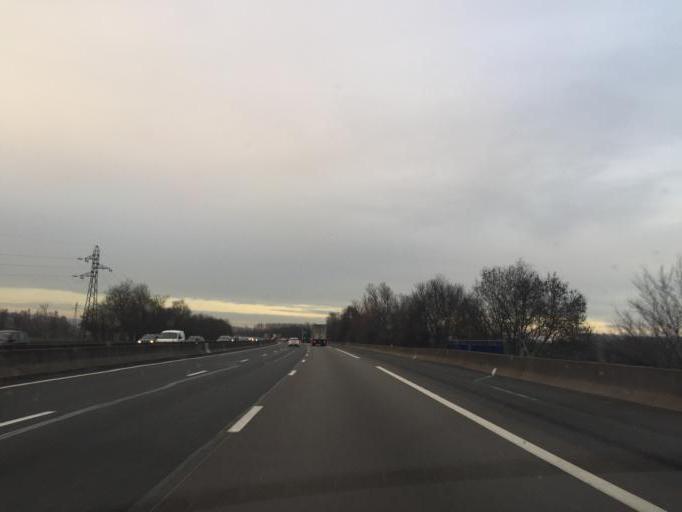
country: FR
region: Bourgogne
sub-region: Departement de Saone-et-Loire
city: Creches-sur-Saone
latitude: 46.2493
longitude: 4.7989
